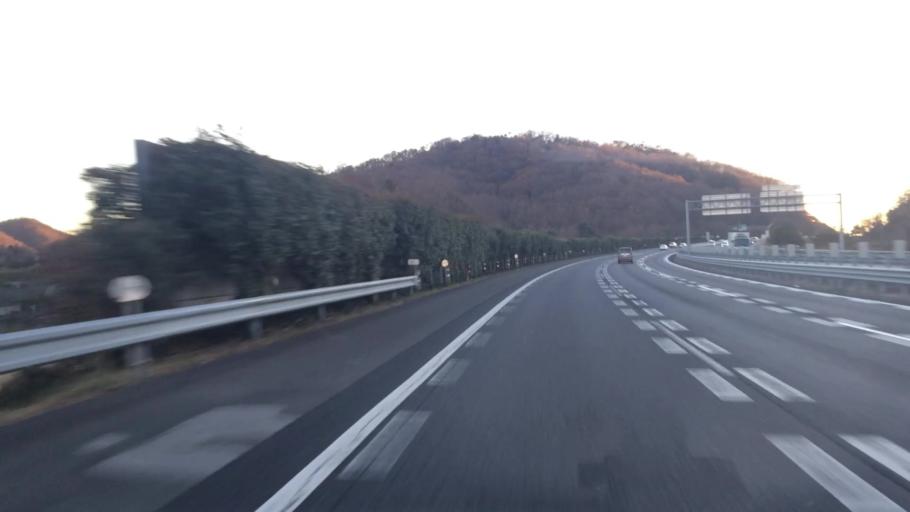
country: JP
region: Tochigi
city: Sano
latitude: 36.3393
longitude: 139.6235
